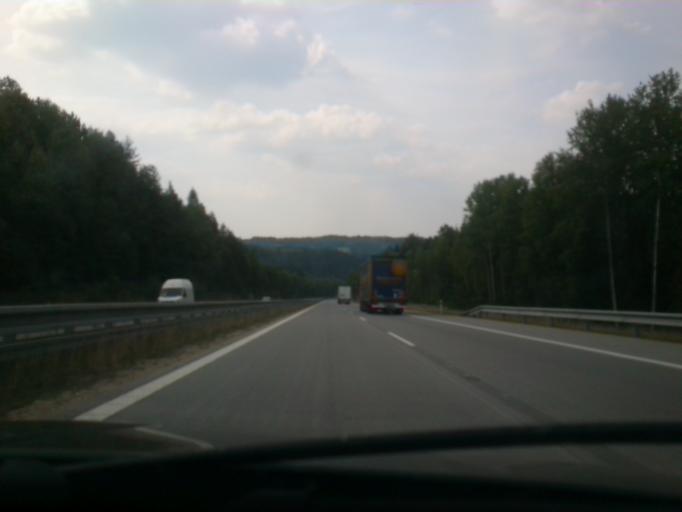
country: CZ
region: Central Bohemia
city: Divisov
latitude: 49.7704
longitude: 14.9441
